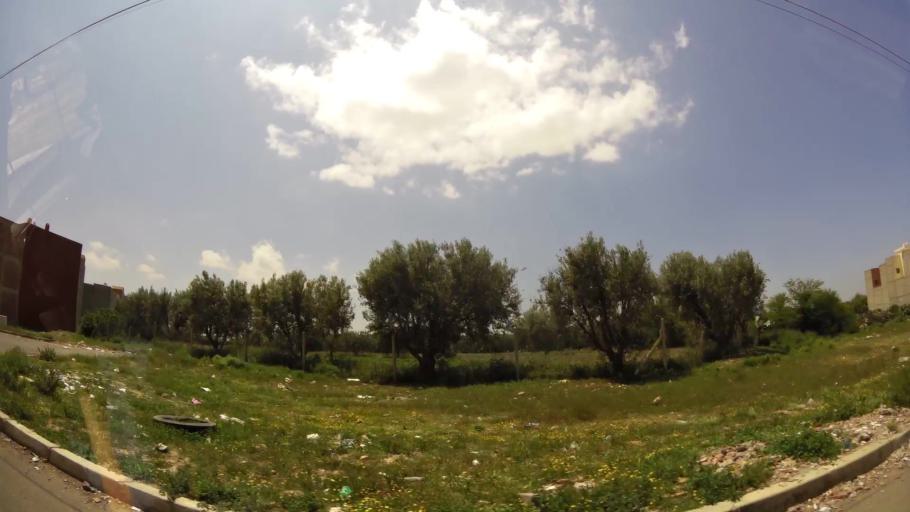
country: MA
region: Oriental
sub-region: Oujda-Angad
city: Oujda
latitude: 34.6939
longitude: -1.8929
